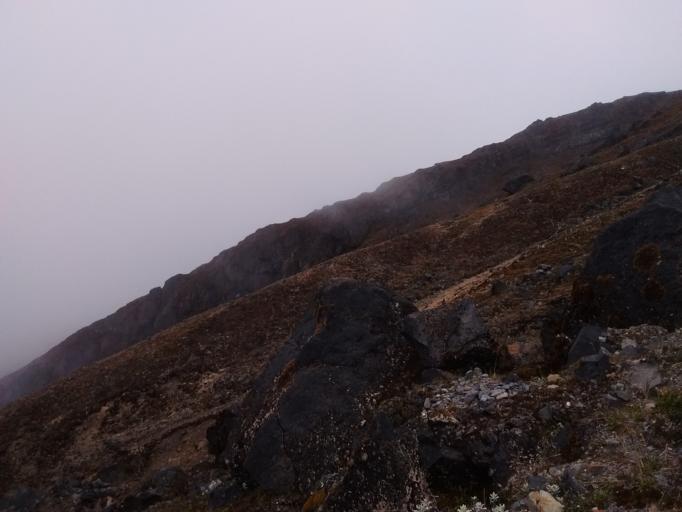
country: CO
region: Cauca
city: Totoro
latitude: 2.3259
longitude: -76.3945
